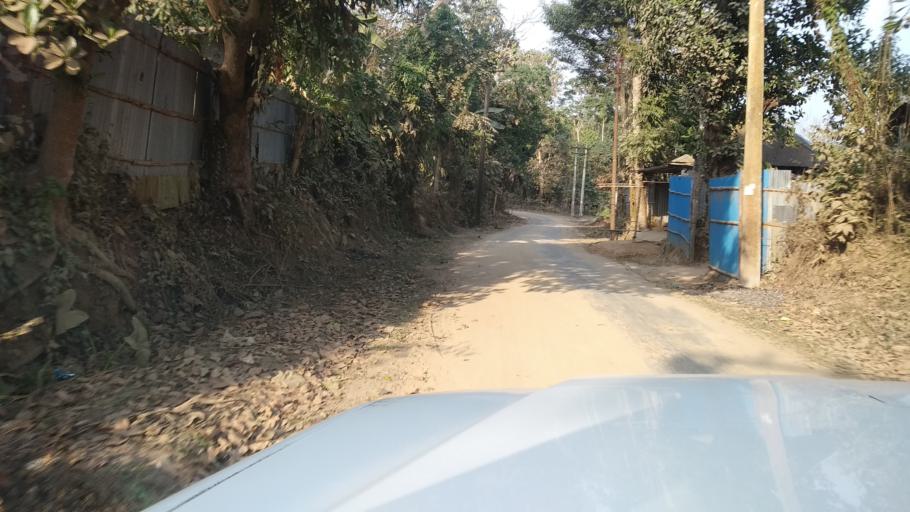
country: IN
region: Tripura
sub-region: West Tripura
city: Sonamura
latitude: 23.4200
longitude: 91.2881
